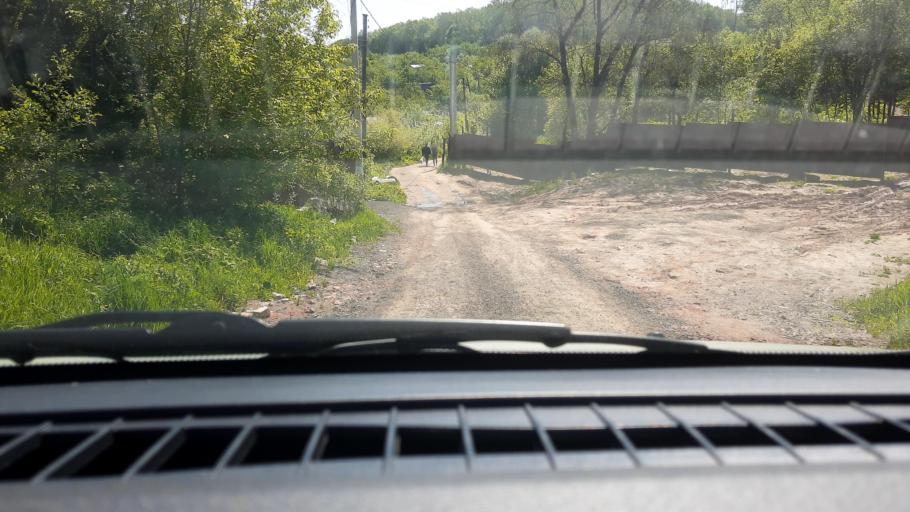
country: RU
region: Nizjnij Novgorod
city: Nizhniy Novgorod
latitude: 56.2906
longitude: 44.0150
